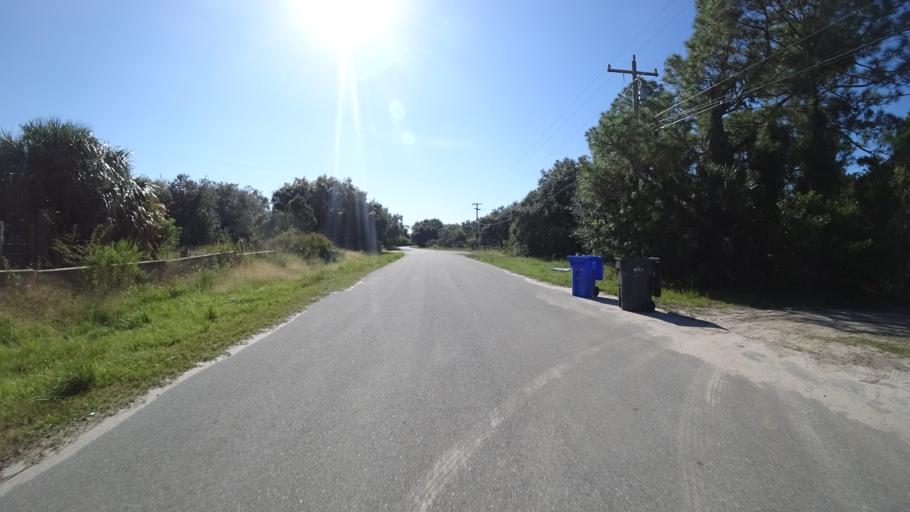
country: US
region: Florida
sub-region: Hillsborough County
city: Sun City Center
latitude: 27.6476
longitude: -82.3488
